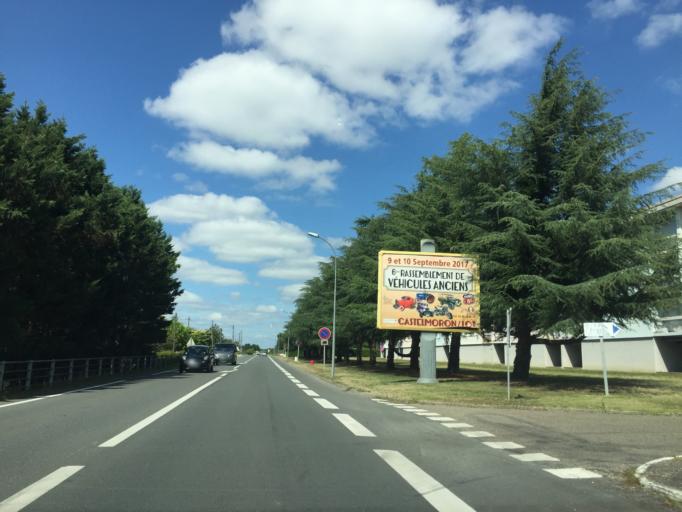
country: FR
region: Aquitaine
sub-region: Departement du Lot-et-Garonne
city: Casteljaloux
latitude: 44.3201
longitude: 0.0946
